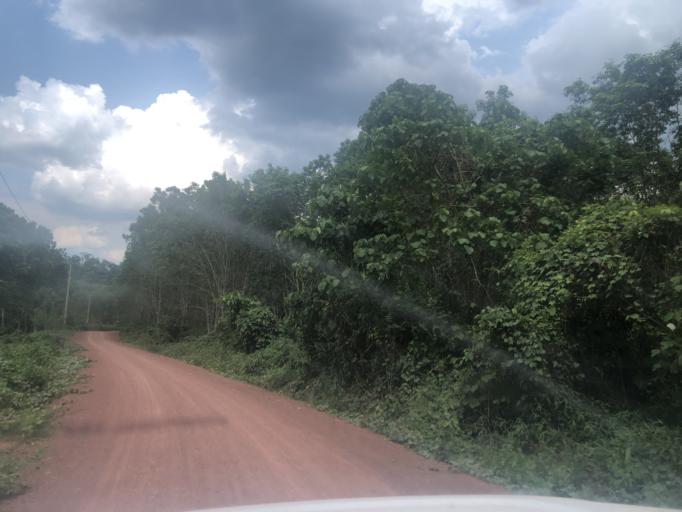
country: LA
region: Phongsali
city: Phongsali
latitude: 21.3048
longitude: 101.9743
